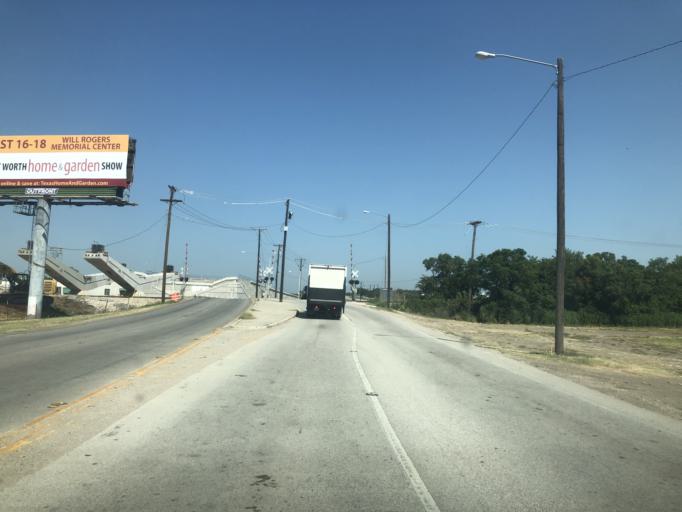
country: US
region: Texas
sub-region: Tarrant County
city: Fort Worth
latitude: 32.7618
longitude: -97.3460
